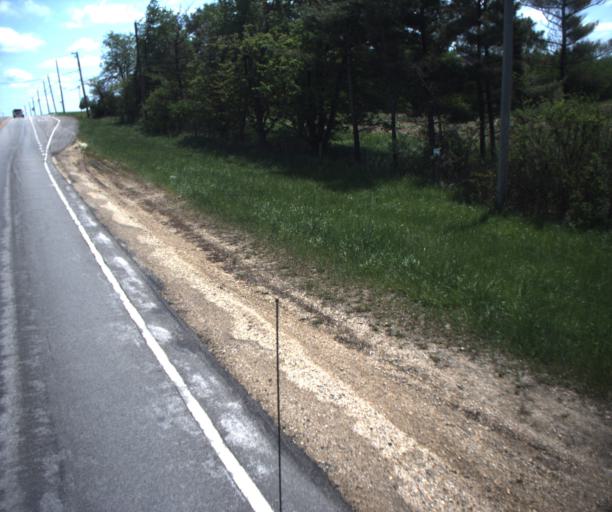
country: US
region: Illinois
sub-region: Kane County
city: Batavia
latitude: 41.8649
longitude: -88.3585
